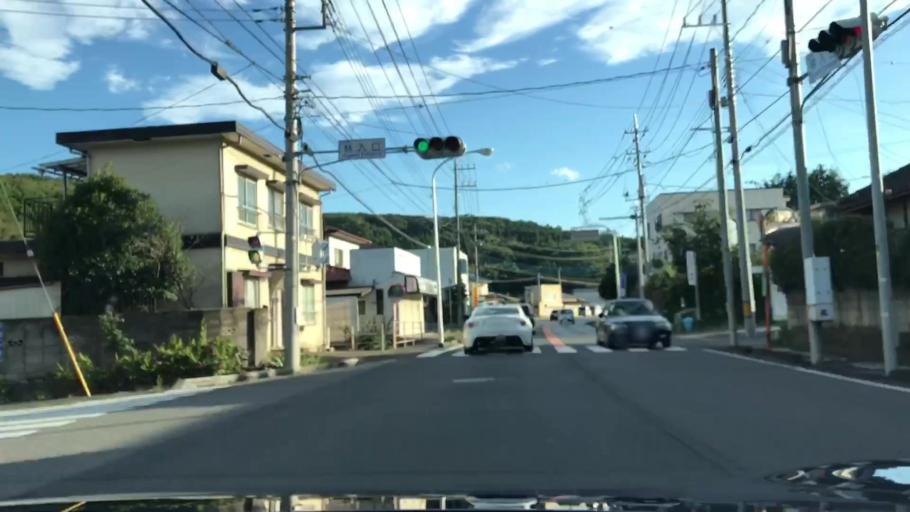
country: JP
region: Tochigi
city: Motegi
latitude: 36.5347
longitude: 140.2061
